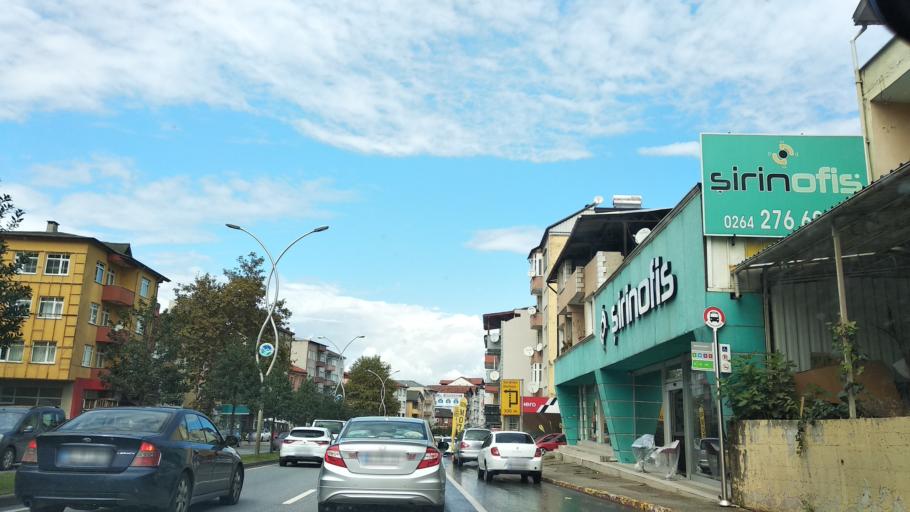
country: TR
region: Sakarya
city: Adapazari
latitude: 40.7511
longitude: 30.3847
